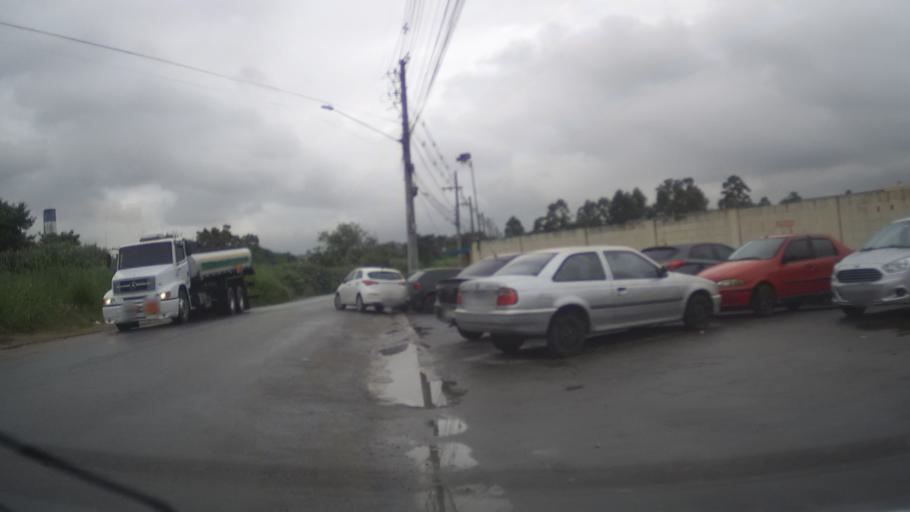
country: BR
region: Sao Paulo
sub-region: Guarulhos
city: Guarulhos
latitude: -23.4782
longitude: -46.4607
